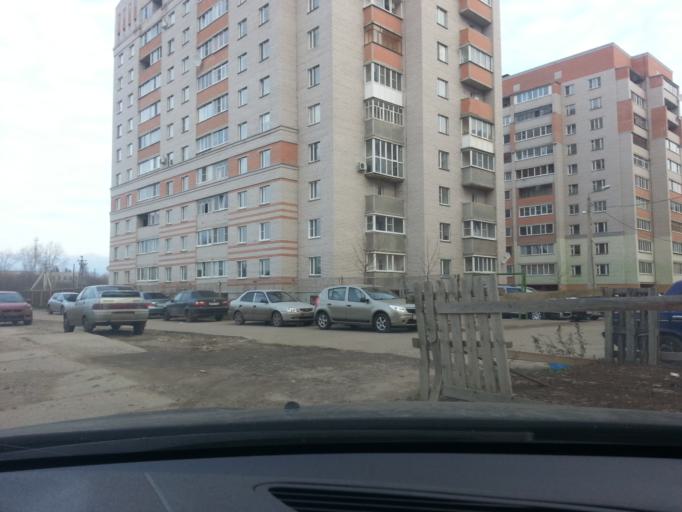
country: RU
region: Vologda
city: Vologda
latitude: 59.2242
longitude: 39.9308
